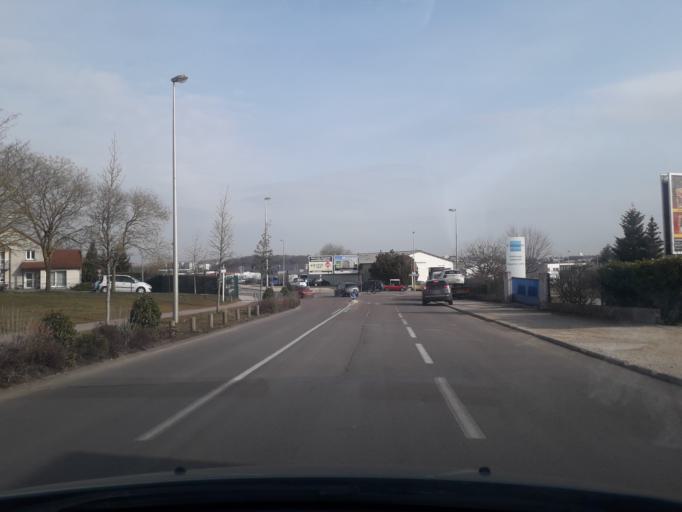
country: FR
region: Bourgogne
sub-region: Departement de la Cote-d'Or
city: Fontaine-les-Dijon
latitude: 47.3505
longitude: 5.0294
